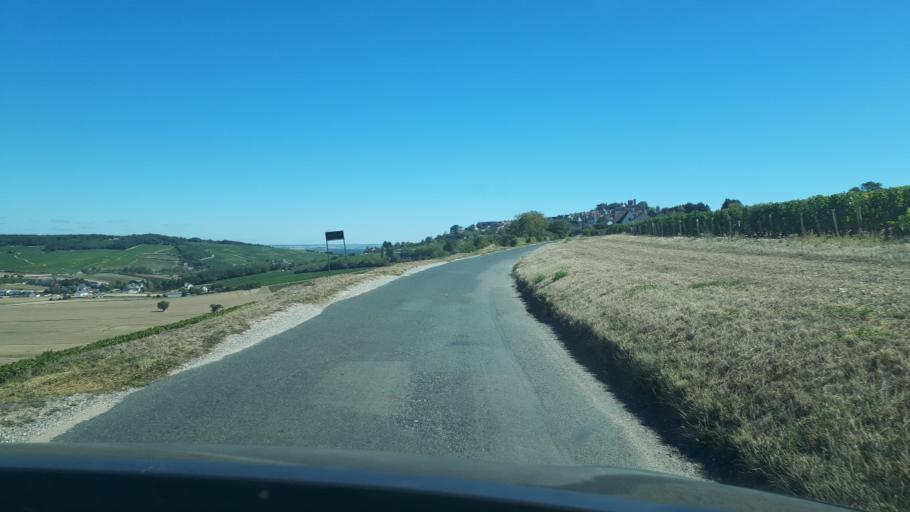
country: FR
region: Centre
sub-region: Departement du Cher
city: Sancerre
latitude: 47.3270
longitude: 2.8203
